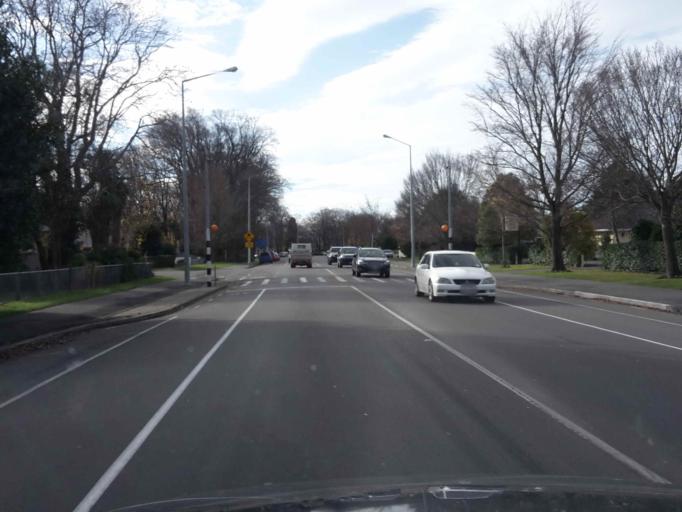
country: NZ
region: Canterbury
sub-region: Selwyn District
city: Prebbleton
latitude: -43.5338
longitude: 172.5642
